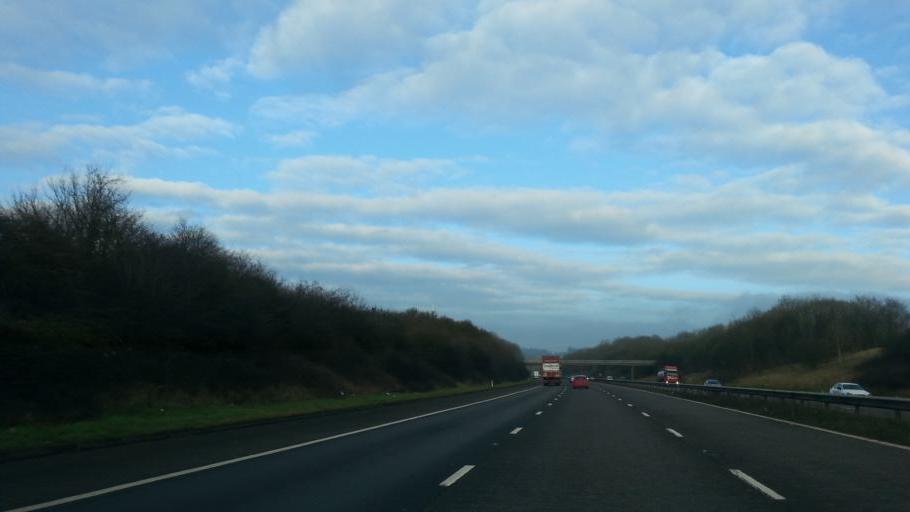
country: GB
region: England
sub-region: South Gloucestershire
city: Charfield
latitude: 51.6670
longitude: -2.4112
